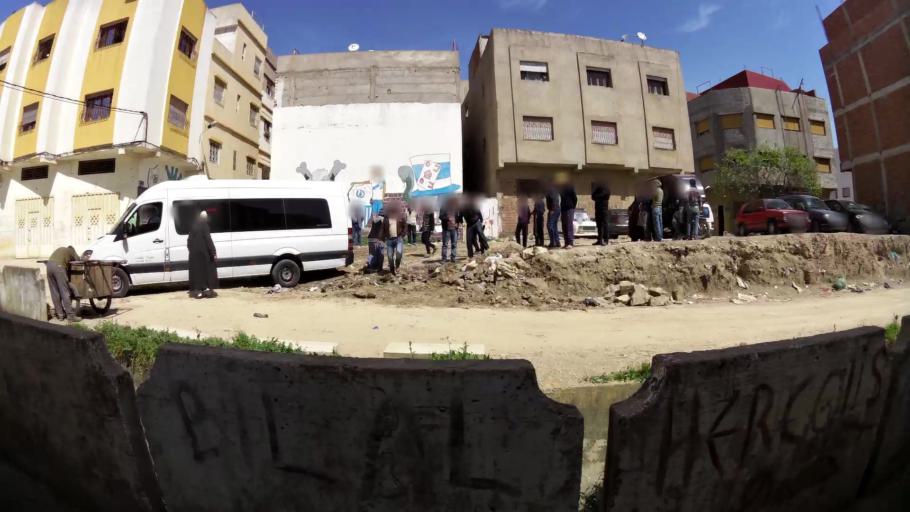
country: MA
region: Tanger-Tetouan
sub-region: Tanger-Assilah
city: Tangier
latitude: 35.7362
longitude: -5.8070
